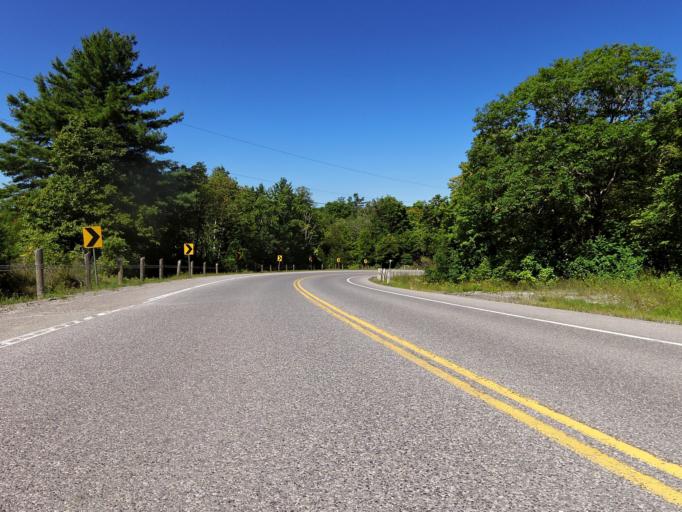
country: CA
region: Ontario
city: Arnprior
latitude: 45.1548
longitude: -76.5177
